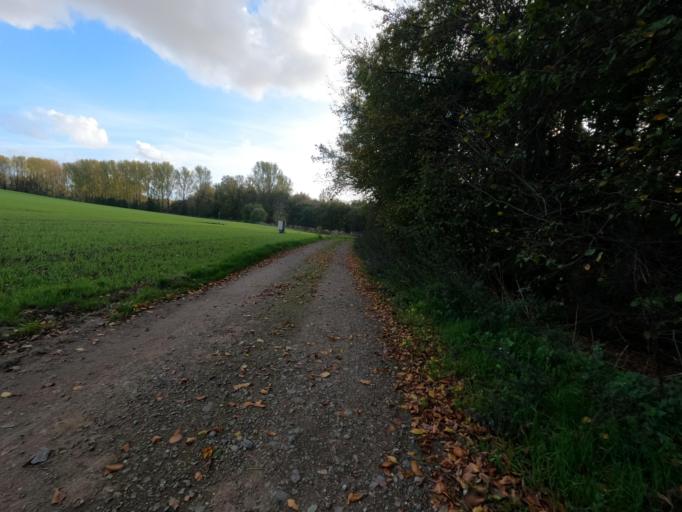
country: DE
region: North Rhine-Westphalia
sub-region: Regierungsbezirk Koln
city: Titz
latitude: 51.0887
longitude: 6.4077
